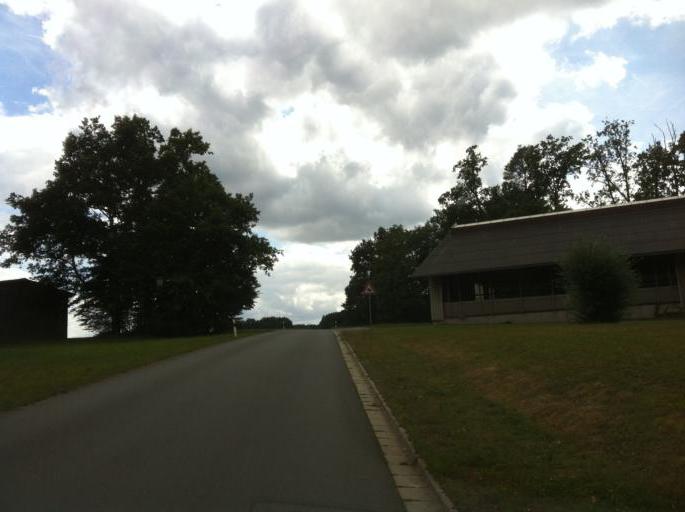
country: DE
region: Bavaria
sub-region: Upper Franconia
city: Harsdorf
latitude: 50.0044
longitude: 11.5547
